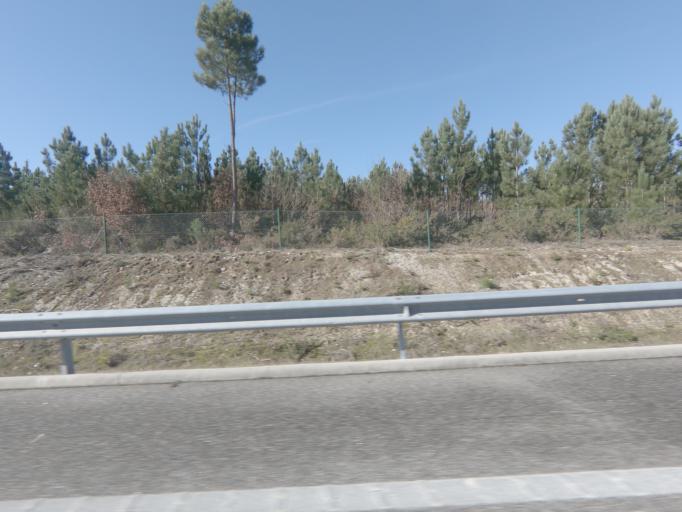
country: ES
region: Galicia
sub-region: Provincia de Ourense
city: Pinor
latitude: 42.4833
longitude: -8.0215
